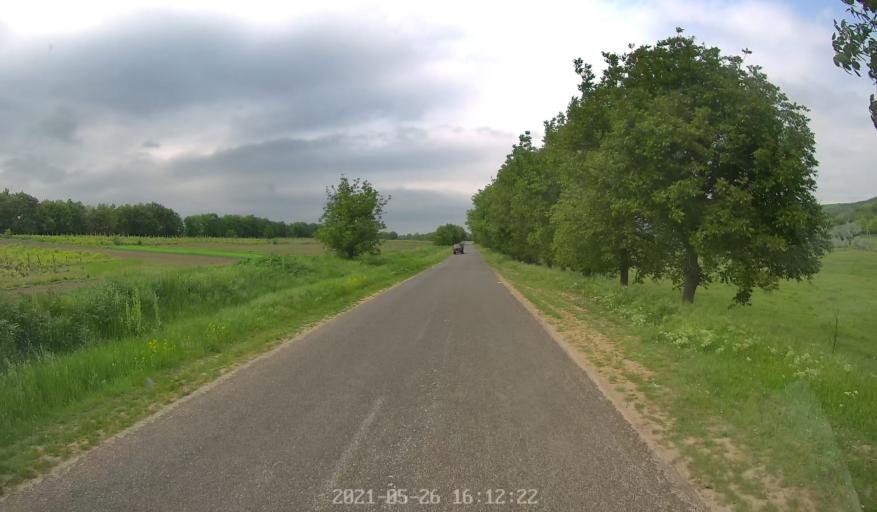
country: MD
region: Hincesti
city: Dancu
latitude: 46.6902
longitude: 28.3361
